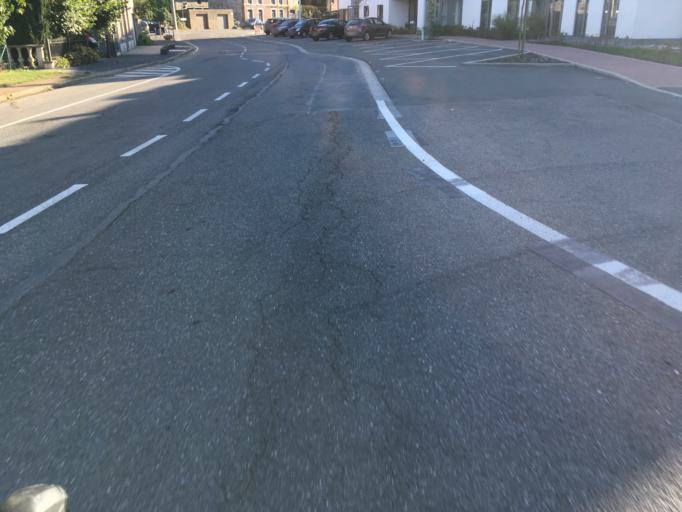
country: BE
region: Wallonia
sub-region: Province de Namur
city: Floreffe
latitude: 50.4357
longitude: 4.7580
